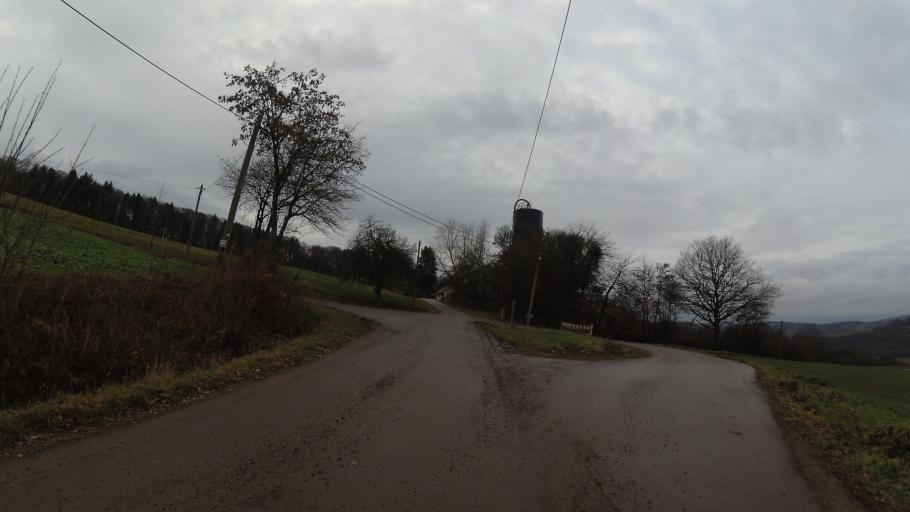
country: DE
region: Rheinland-Pfalz
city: Breitenbach
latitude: 49.4424
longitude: 7.2599
